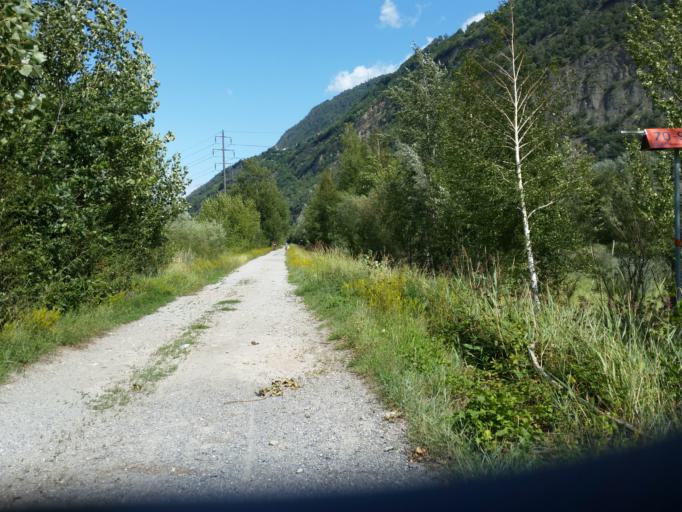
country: CH
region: Valais
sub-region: Martigny District
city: Riddes
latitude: 46.1821
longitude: 7.2386
